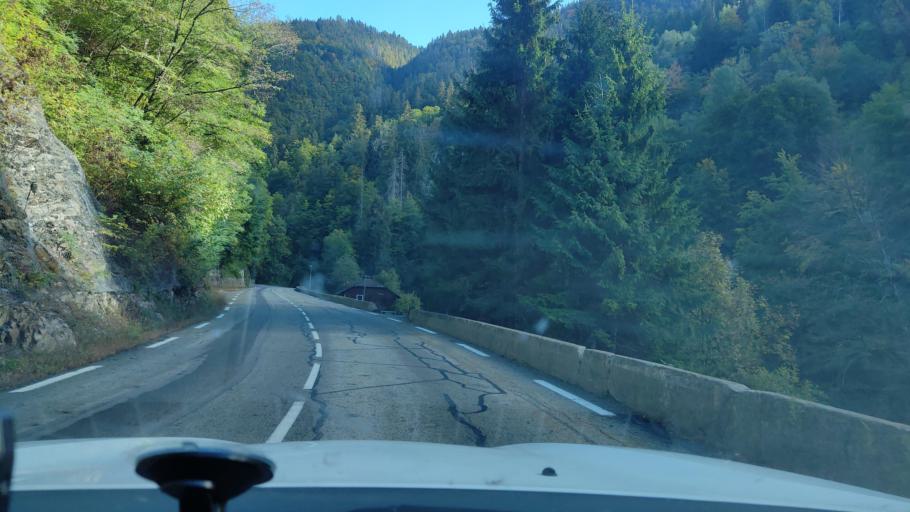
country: FR
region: Rhone-Alpes
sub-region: Departement de la Savoie
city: Ugine
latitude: 45.7714
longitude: 6.4830
